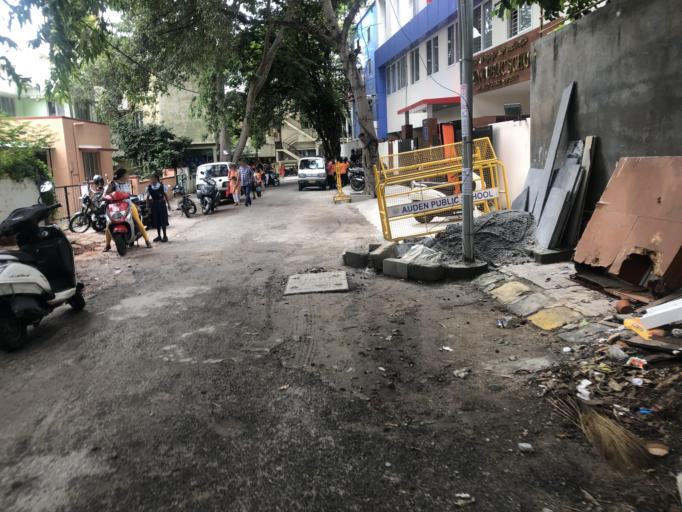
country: IN
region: Karnataka
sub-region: Bangalore Urban
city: Bangalore
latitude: 12.9379
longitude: 77.5435
